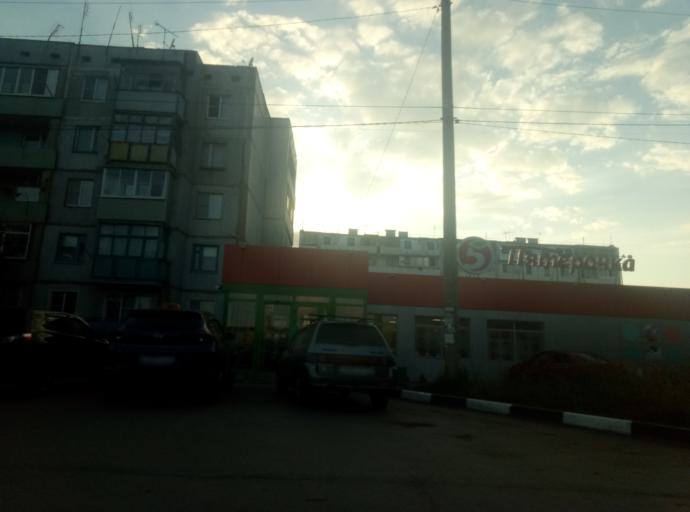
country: RU
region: Tula
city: Kireyevsk
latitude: 53.9202
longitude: 37.9152
